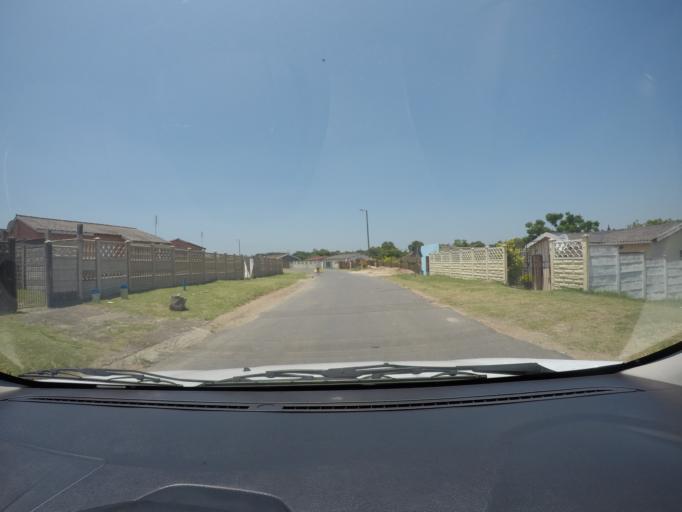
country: ZA
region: KwaZulu-Natal
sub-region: uThungulu District Municipality
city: eSikhawini
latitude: -28.8769
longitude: 31.9076
